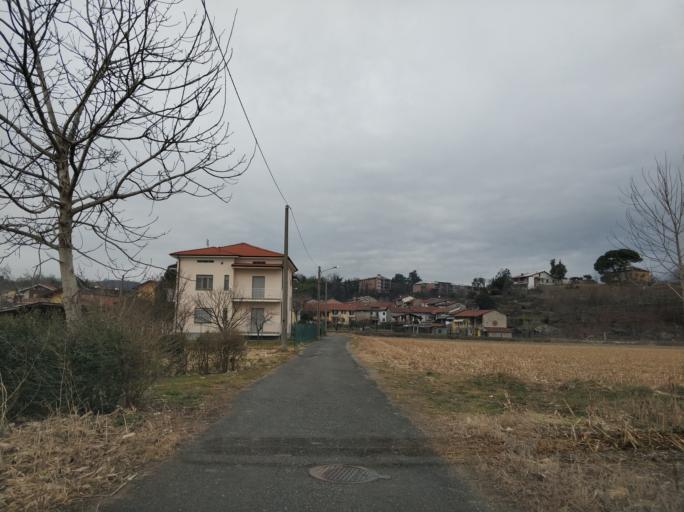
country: IT
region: Piedmont
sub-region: Provincia di Torino
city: Ivrea
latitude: 45.4446
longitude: 7.8819
